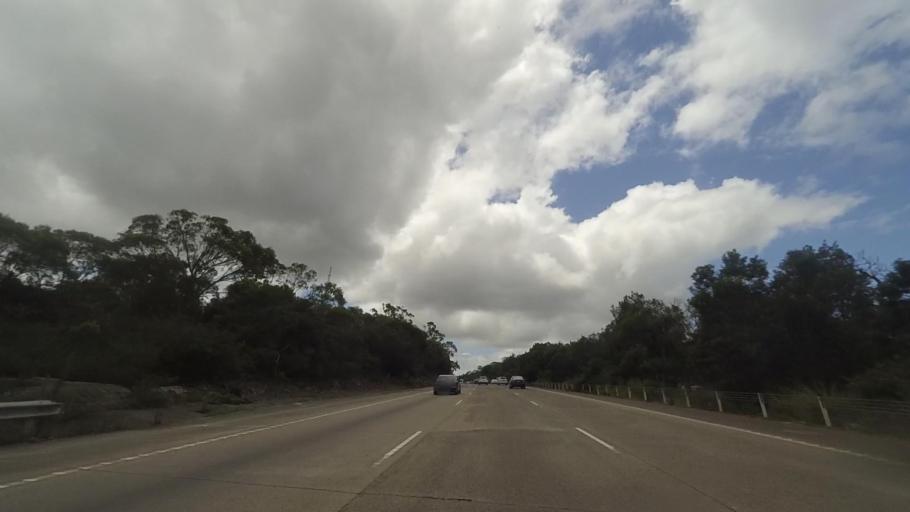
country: AU
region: New South Wales
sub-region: Gosford Shire
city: Point Clare
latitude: -33.4134
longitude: 151.2977
